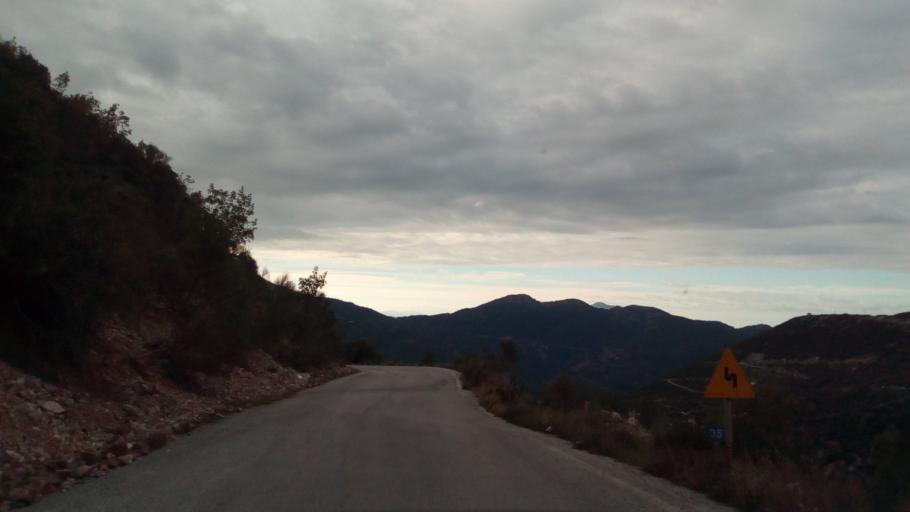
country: GR
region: West Greece
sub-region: Nomos Aitolias kai Akarnanias
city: Thermo
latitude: 38.6039
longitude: 21.8033
